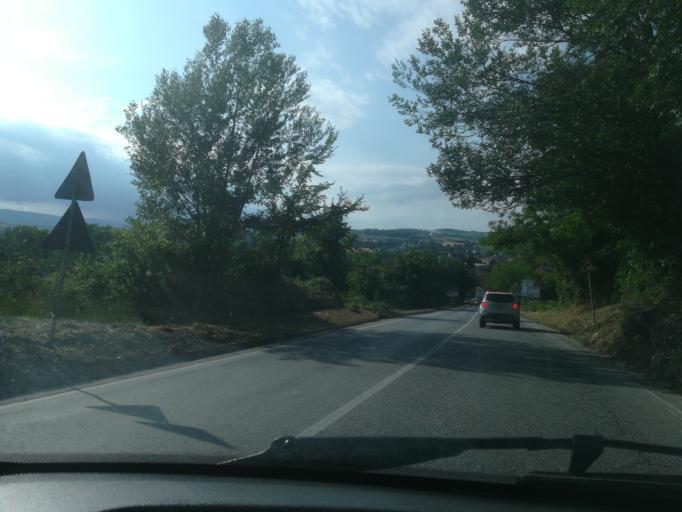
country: IT
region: The Marches
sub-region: Provincia di Macerata
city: Villa Potenza
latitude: 43.3181
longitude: 13.4288
